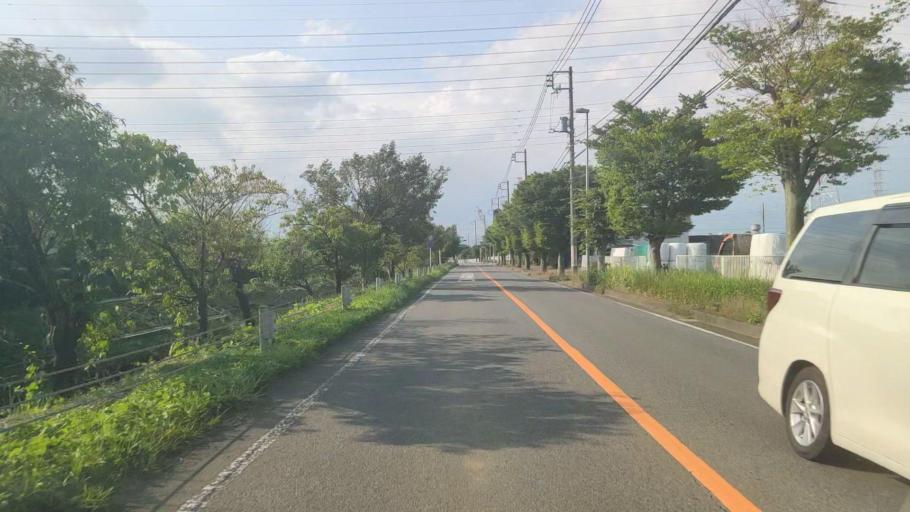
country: JP
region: Kanagawa
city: Isehara
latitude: 35.3967
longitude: 139.3379
